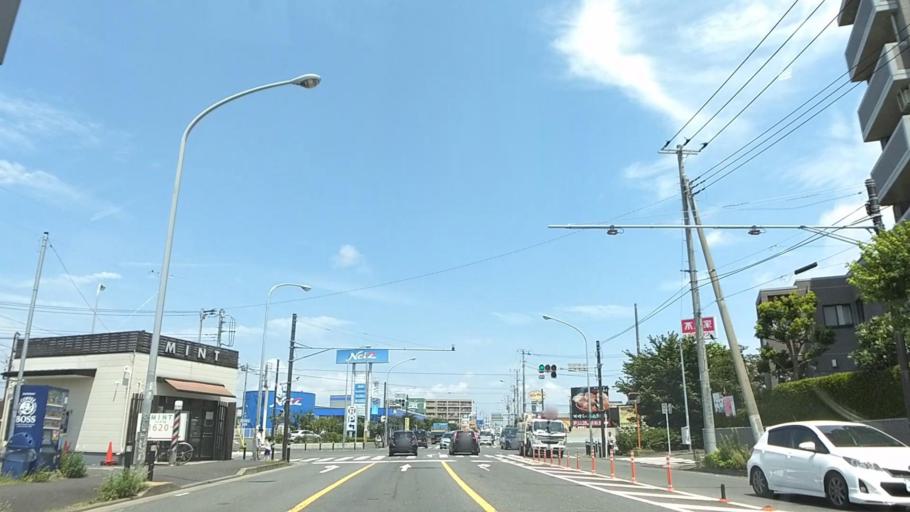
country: JP
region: Kanagawa
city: Minami-rinkan
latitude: 35.4582
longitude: 139.4808
